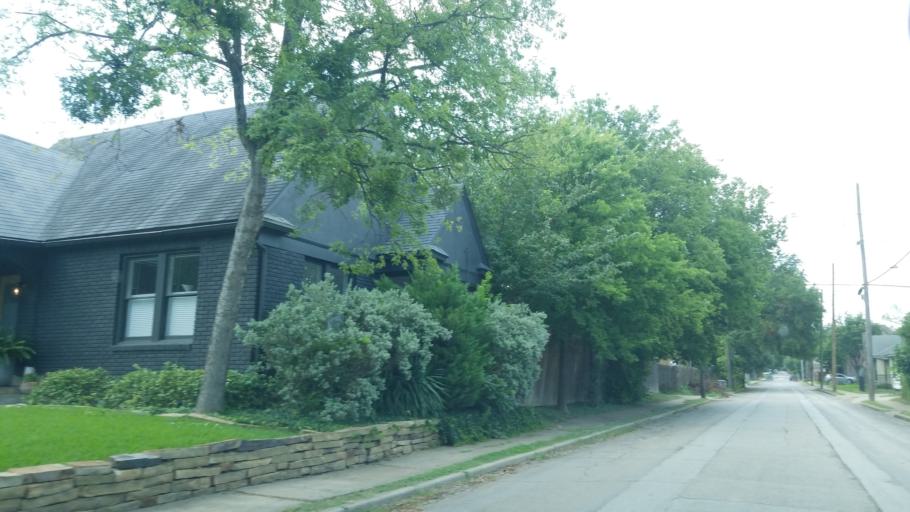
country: US
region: Texas
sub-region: Dallas County
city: Highland Park
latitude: 32.8234
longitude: -96.7823
